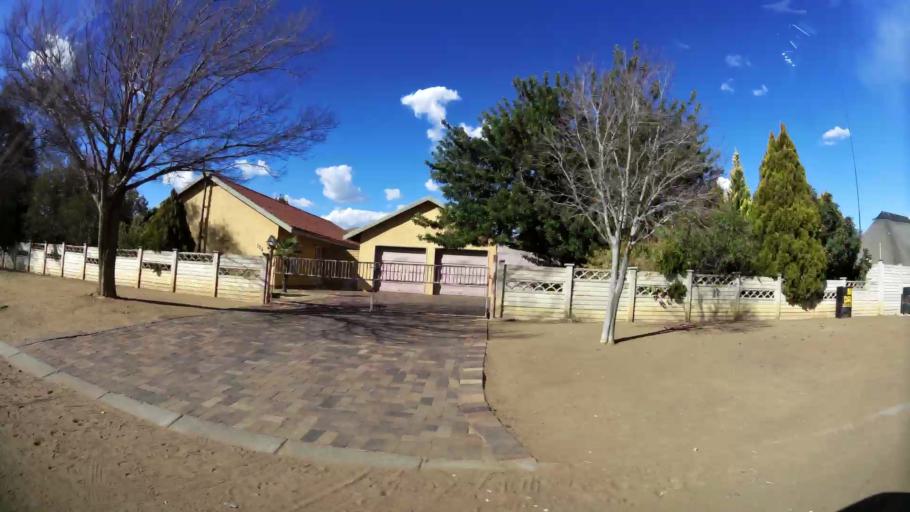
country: ZA
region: North-West
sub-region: Dr Kenneth Kaunda District Municipality
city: Klerksdorp
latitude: -26.8217
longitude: 26.6575
